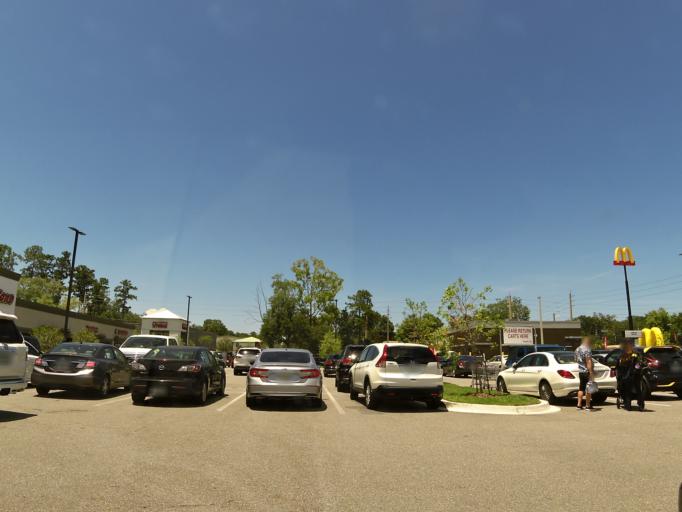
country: US
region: Florida
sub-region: Saint Johns County
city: Fruit Cove
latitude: 30.1599
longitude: -81.6334
